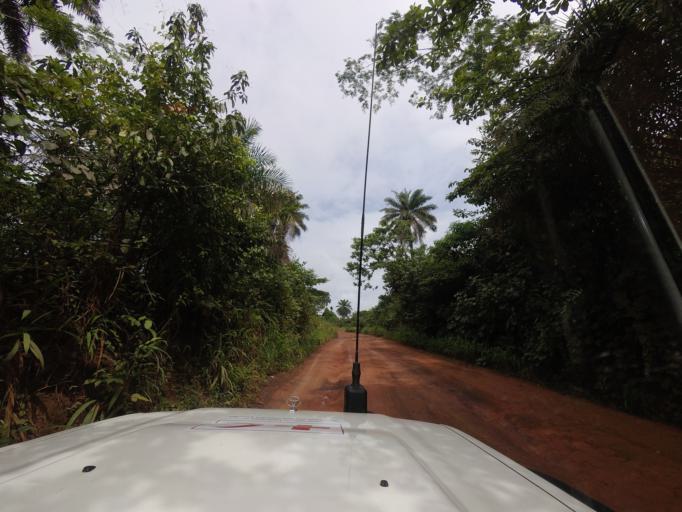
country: GN
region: Nzerekore
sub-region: Nzerekore Prefecture
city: Nzerekore
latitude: 7.7239
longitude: -8.8769
